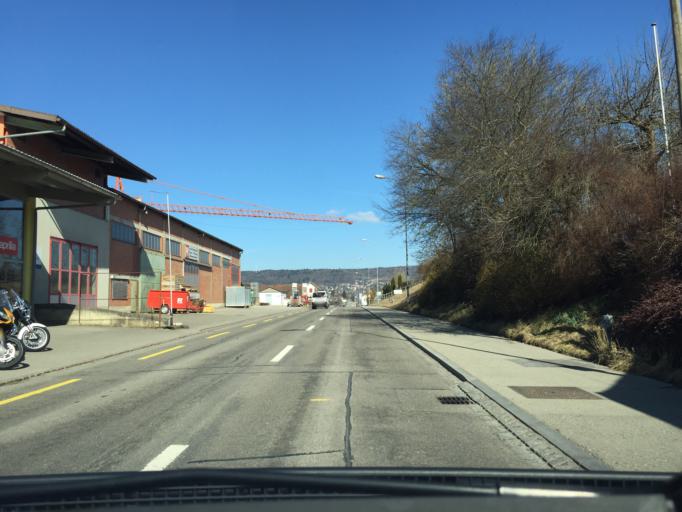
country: CH
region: Thurgau
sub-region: Frauenfeld District
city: Diessenhofen
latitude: 47.6737
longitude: 8.7505
